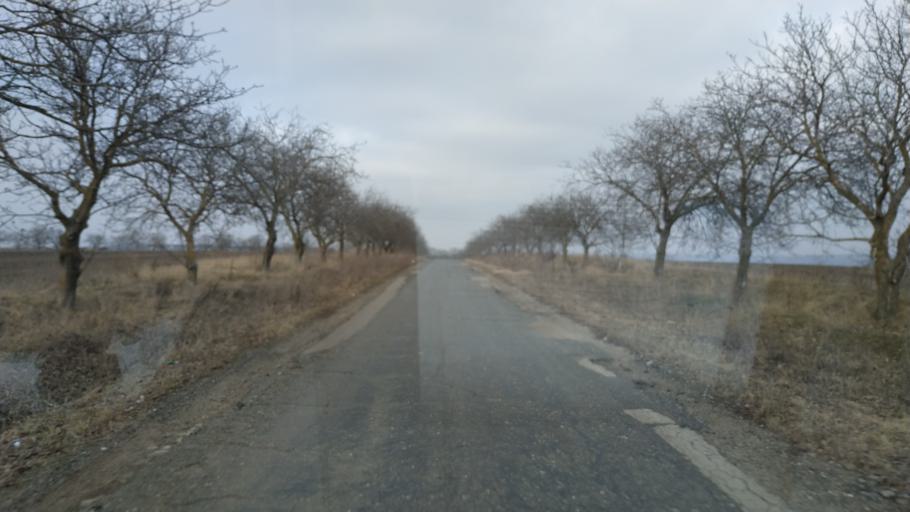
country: MD
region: Hincesti
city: Dancu
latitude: 46.9011
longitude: 28.3052
